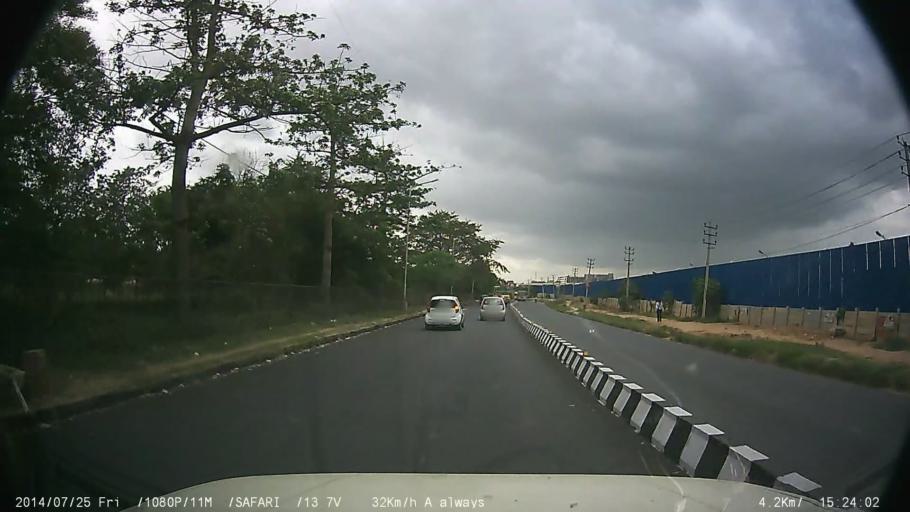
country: IN
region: Karnataka
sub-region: Bangalore Urban
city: Bangalore
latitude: 12.9244
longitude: 77.6469
